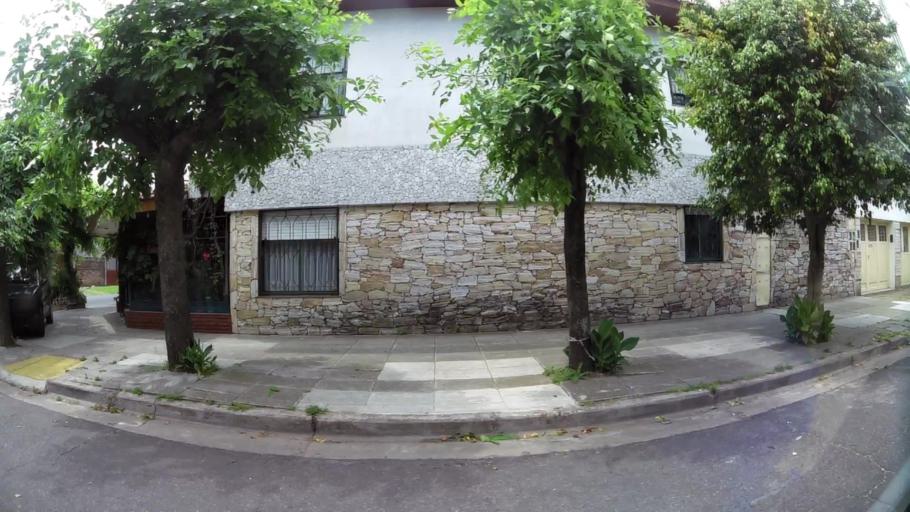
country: AR
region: Buenos Aires
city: San Justo
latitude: -34.6696
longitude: -58.5483
